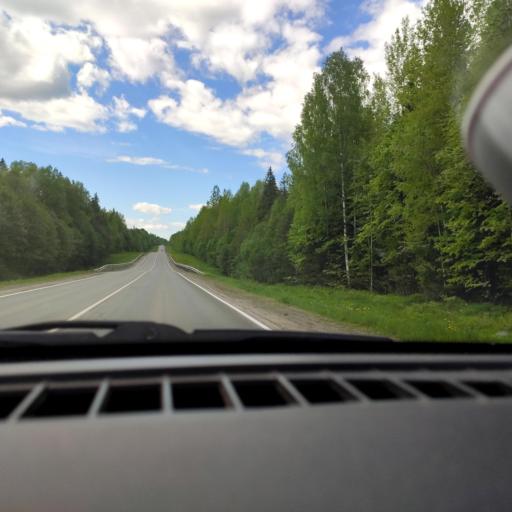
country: RU
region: Perm
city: Perm
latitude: 58.1615
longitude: 56.2448
